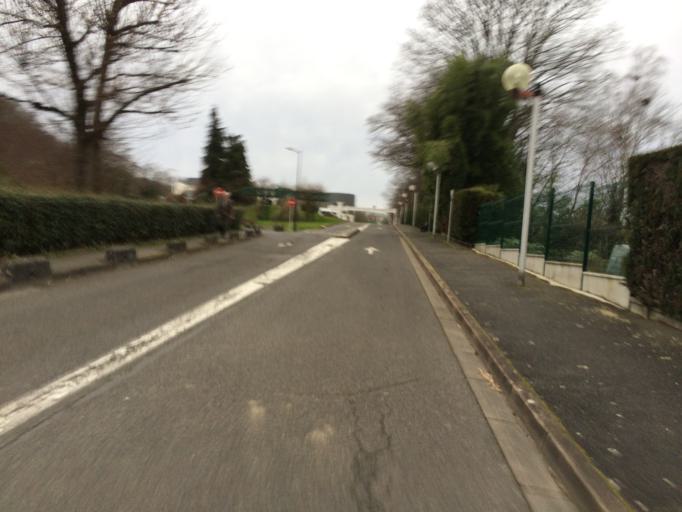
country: FR
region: Ile-de-France
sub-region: Departement de l'Essonne
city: Villebon-sur-Yvette
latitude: 48.6981
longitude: 2.2366
